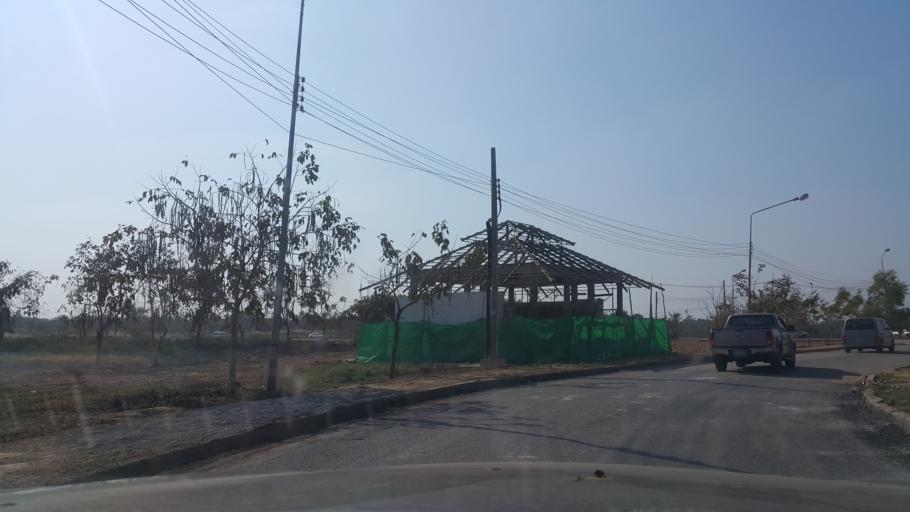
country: TH
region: Khon Kaen
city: Khon Kaen
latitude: 16.5100
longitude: 102.8697
